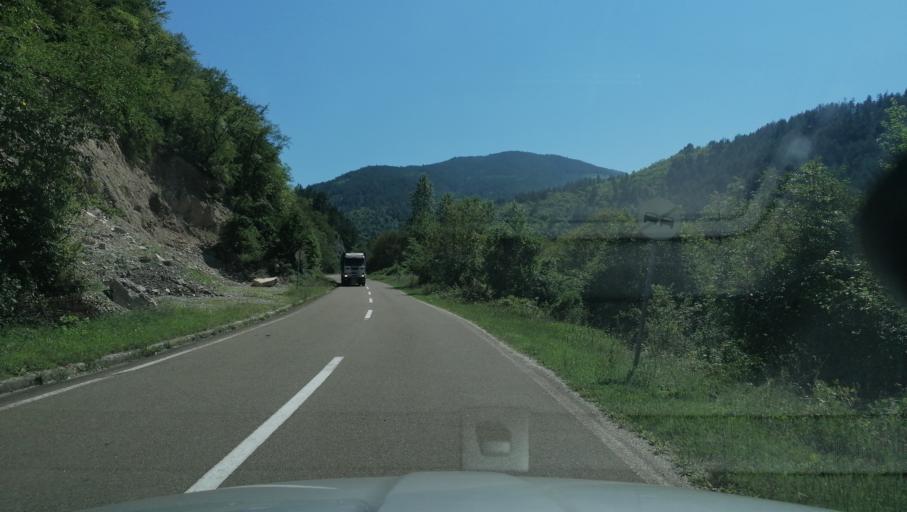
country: RS
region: Central Serbia
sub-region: Raski Okrug
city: Raska
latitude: 43.4769
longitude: 20.5409
